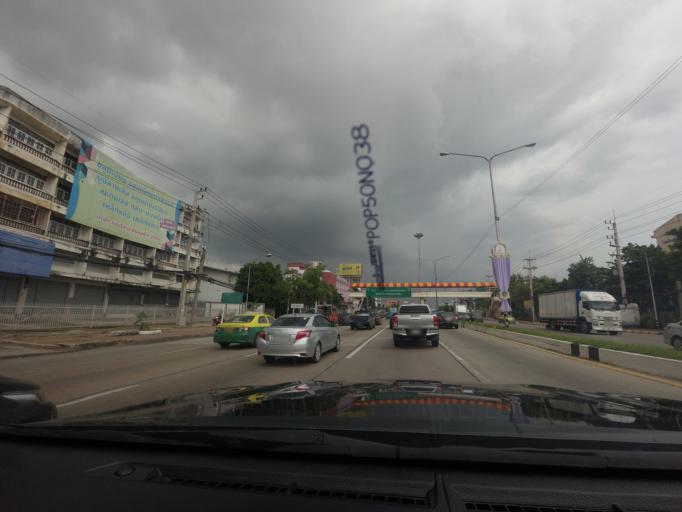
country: TH
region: Bangkok
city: Nong Khaem
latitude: 13.7041
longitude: 100.3235
